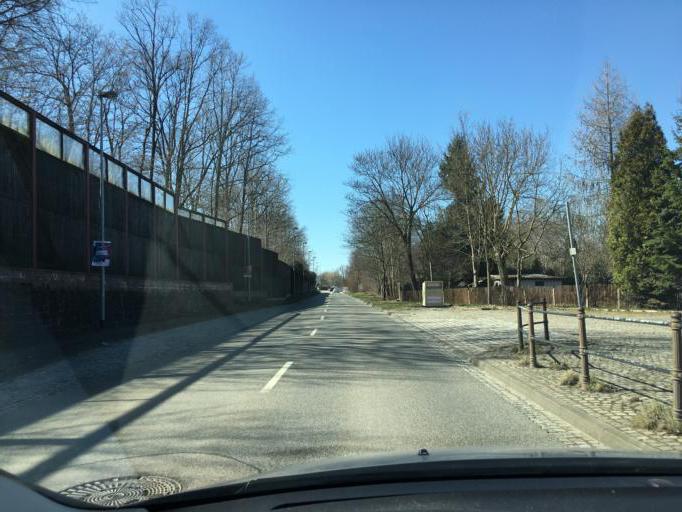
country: DE
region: Saxony
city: Limbach-Oberfrohna
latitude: 50.8610
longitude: 12.7729
